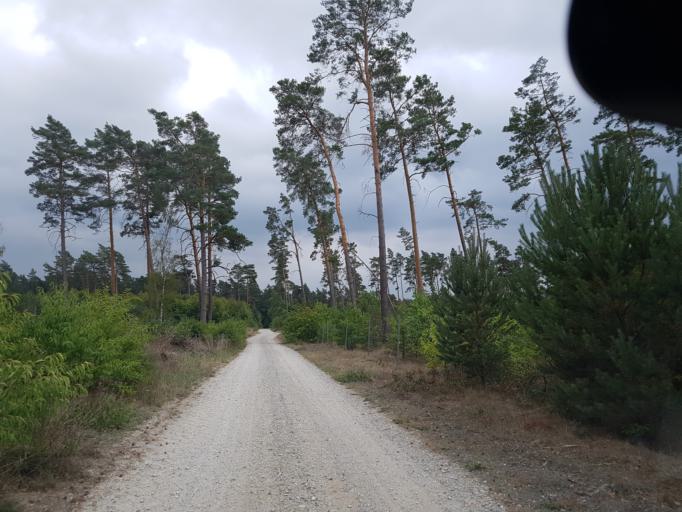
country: DE
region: Saxony-Anhalt
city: Rosslau
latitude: 52.0223
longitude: 12.2908
